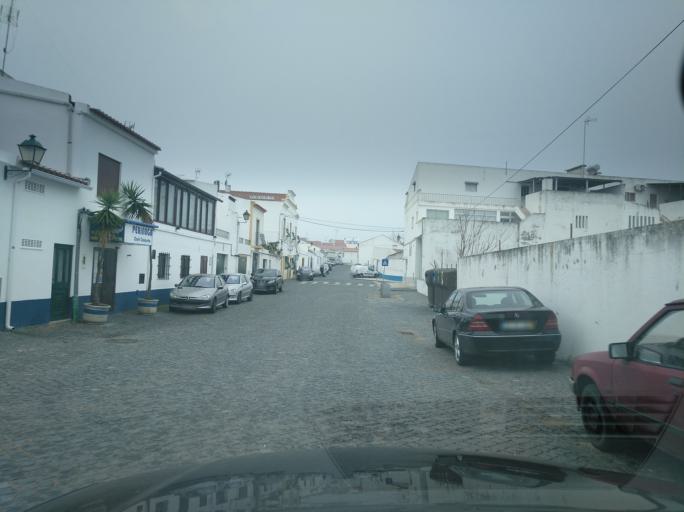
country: PT
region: Portalegre
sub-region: Campo Maior
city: Campo Maior
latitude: 39.0130
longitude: -7.0670
